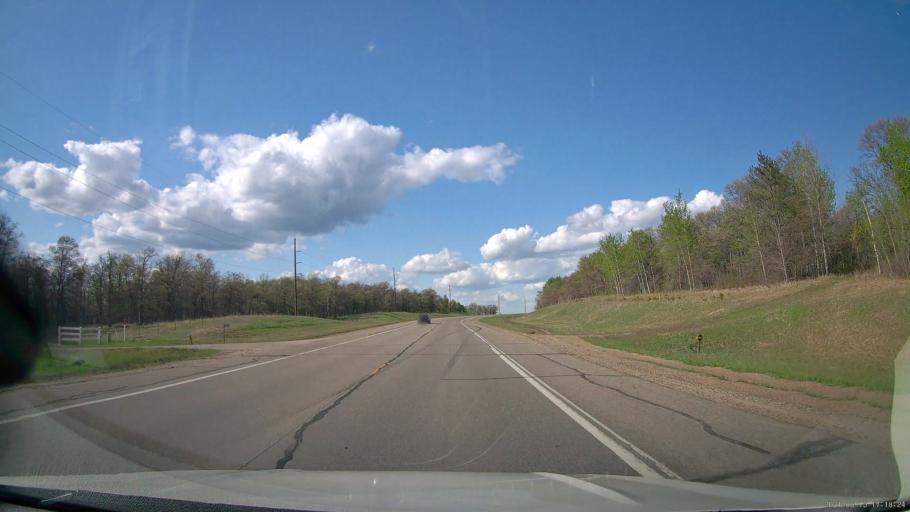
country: US
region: Minnesota
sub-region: Hubbard County
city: Park Rapids
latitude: 46.9608
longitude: -95.0184
